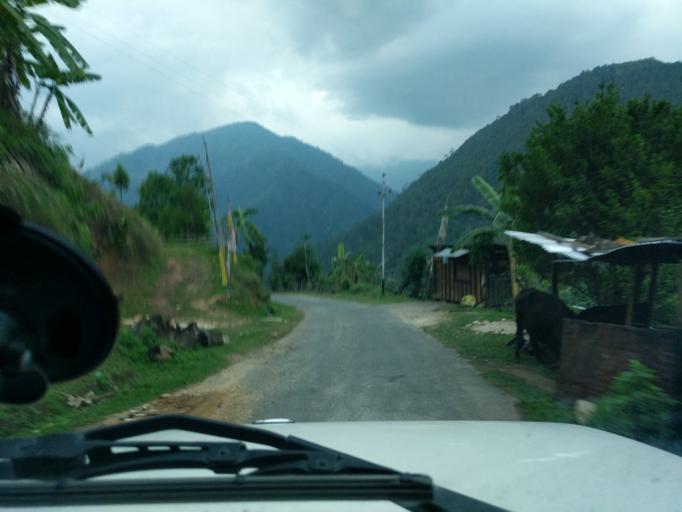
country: BT
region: Mongar
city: Mongar
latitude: 27.2899
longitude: 91.1499
